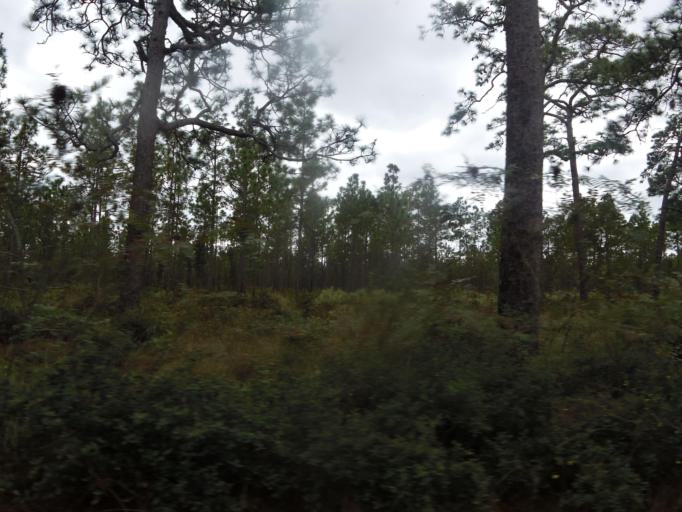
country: US
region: Florida
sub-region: Clay County
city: Keystone Heights
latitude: 29.8468
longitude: -81.9562
